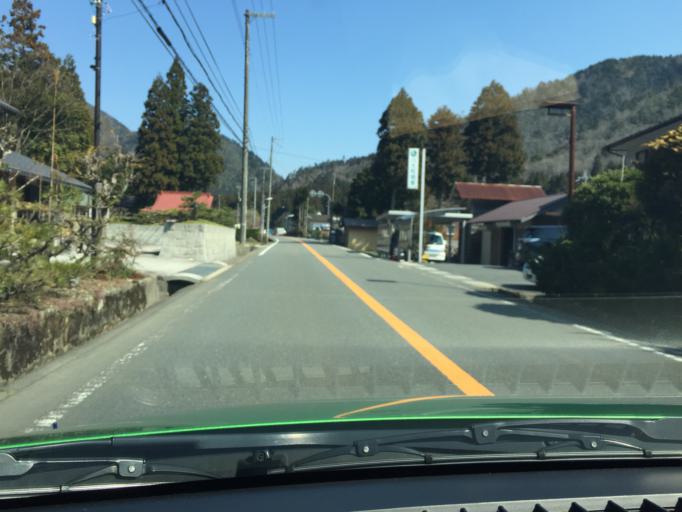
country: JP
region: Kyoto
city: Maizuru
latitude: 35.2809
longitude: 135.5550
